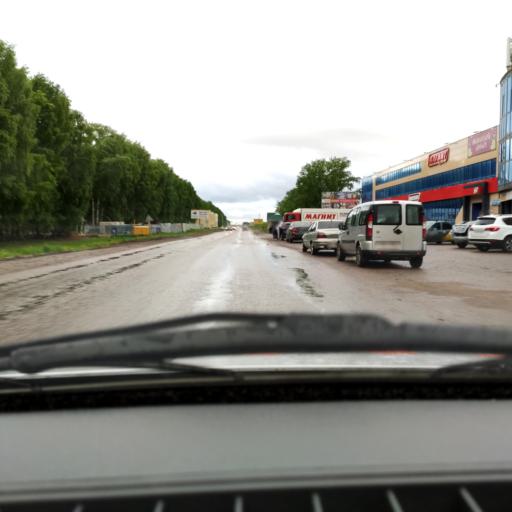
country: RU
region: Bashkortostan
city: Sterlitamak
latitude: 53.5880
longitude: 55.8960
